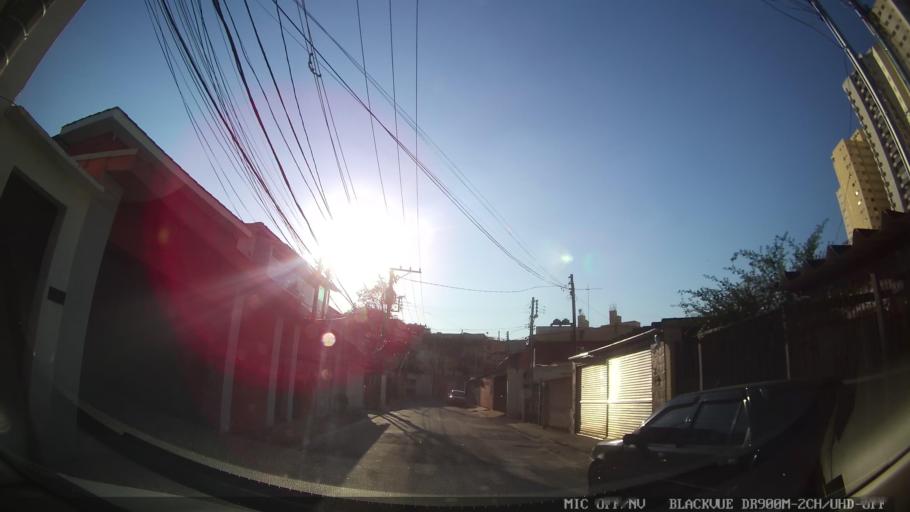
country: BR
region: Sao Paulo
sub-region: Sao Paulo
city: Sao Paulo
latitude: -23.4945
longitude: -46.6396
